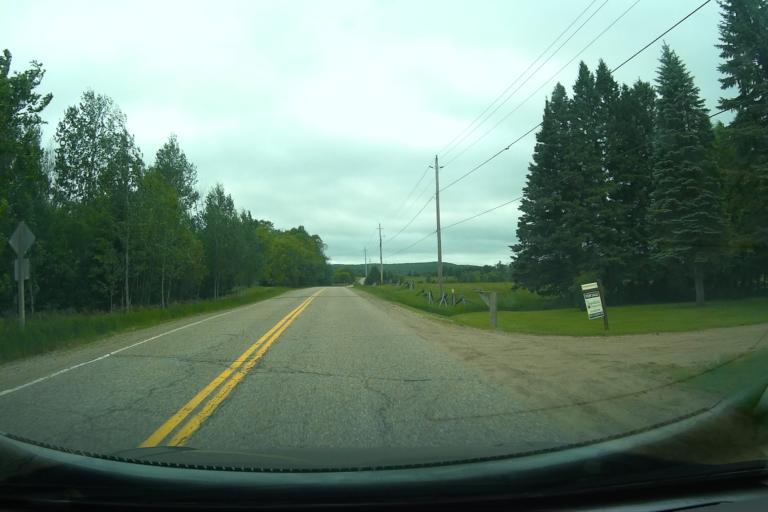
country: CA
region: Ontario
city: Pembroke
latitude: 45.4617
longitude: -77.2623
